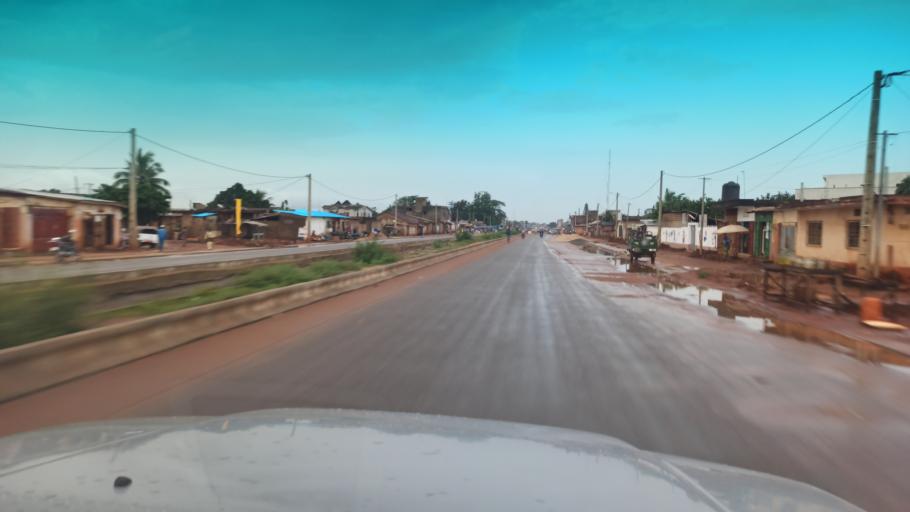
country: BJ
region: Queme
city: Porto-Novo
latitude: 6.4981
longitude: 2.6264
